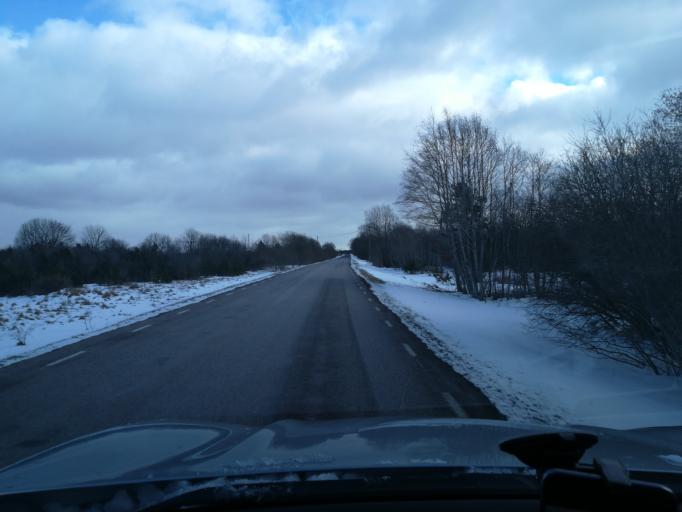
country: EE
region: Harju
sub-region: Keila linn
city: Keila
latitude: 59.4377
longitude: 24.3975
